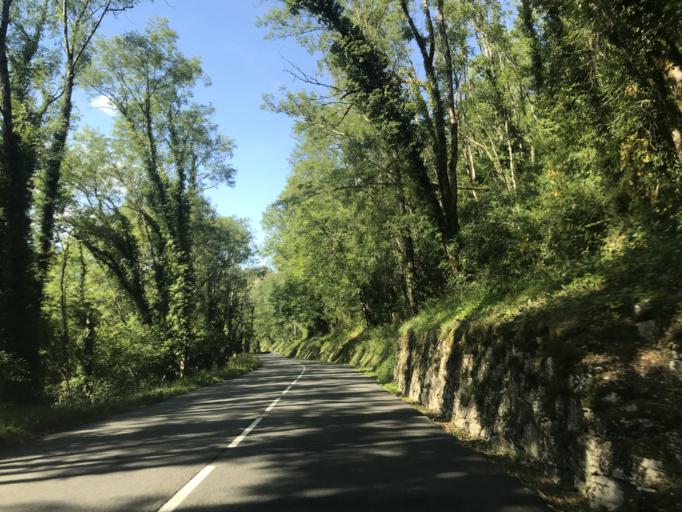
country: FR
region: Rhone-Alpes
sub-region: Departement de l'Ain
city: Culoz
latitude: 45.8006
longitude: 5.7871
